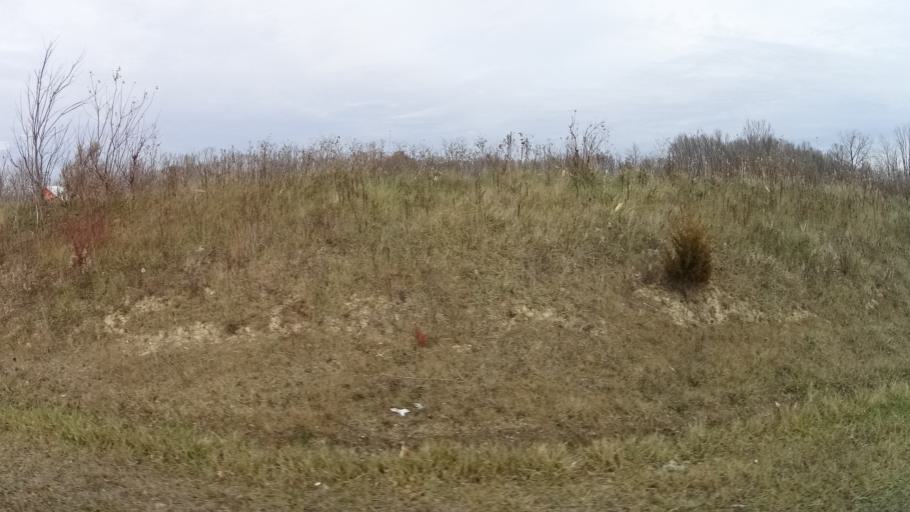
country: US
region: Ohio
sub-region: Lorain County
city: Lagrange
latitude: 41.1367
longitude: -82.1209
